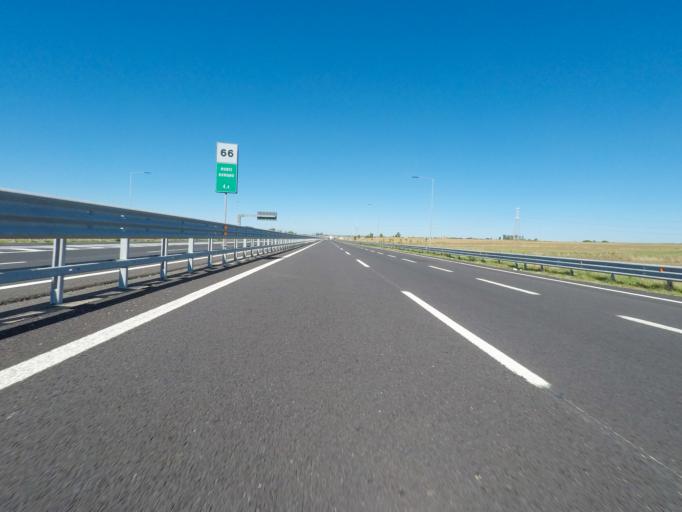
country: IT
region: Latium
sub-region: Citta metropolitana di Roma Capitale
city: Aurelia
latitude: 42.1685
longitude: 11.7879
